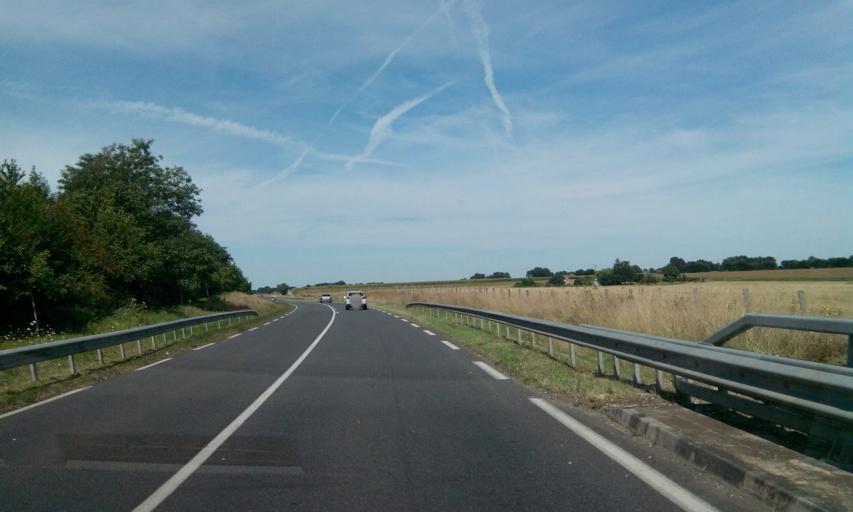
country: FR
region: Poitou-Charentes
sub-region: Departement de la Vienne
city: Charroux
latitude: 46.1530
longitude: 0.3989
